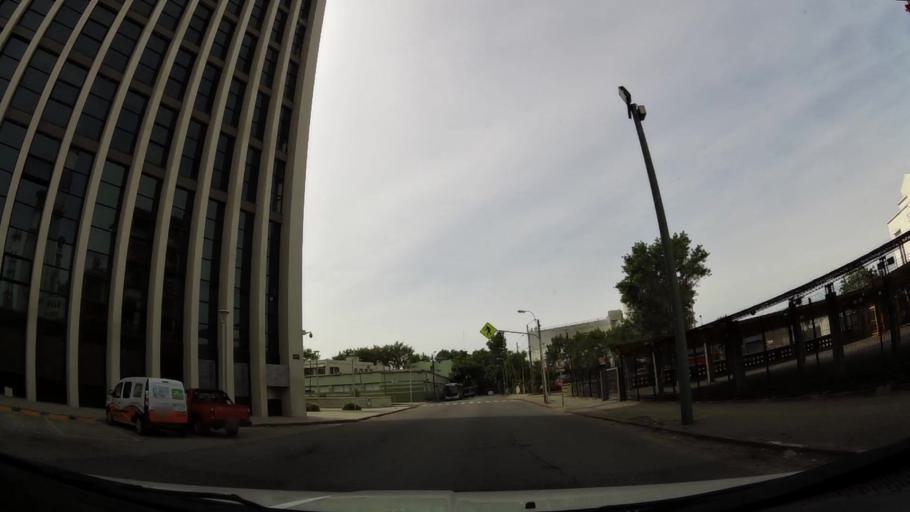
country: UY
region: Montevideo
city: Montevideo
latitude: -34.8856
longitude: -56.1956
